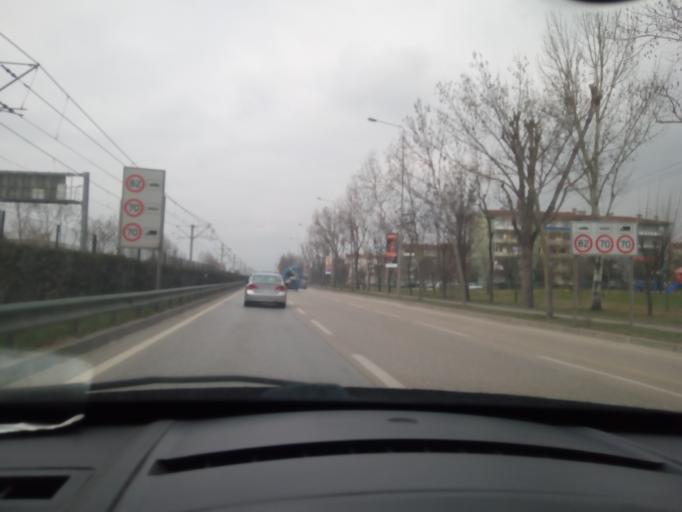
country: TR
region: Bursa
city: Niluefer
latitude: 40.2403
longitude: 28.9713
